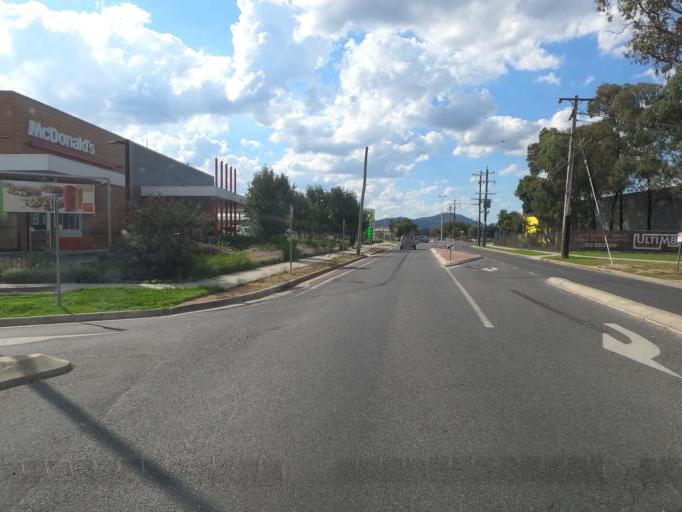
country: AU
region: New South Wales
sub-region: Albury Municipality
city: East Albury
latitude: -36.0757
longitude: 146.9476
